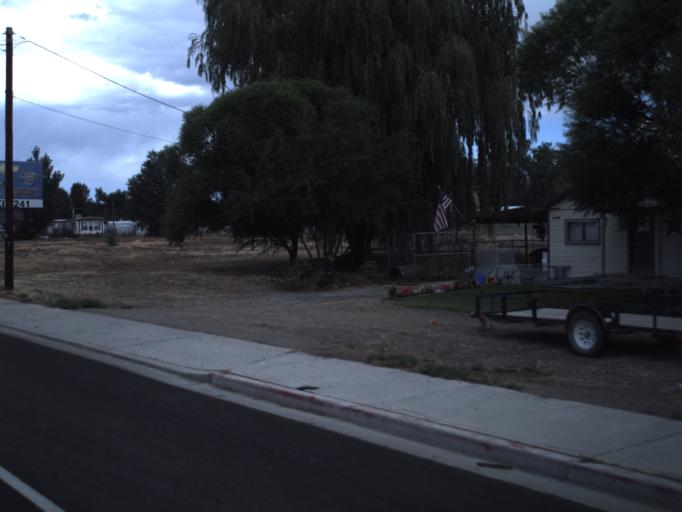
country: US
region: Utah
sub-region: Carbon County
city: Wellington
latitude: 39.5425
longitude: -110.7245
